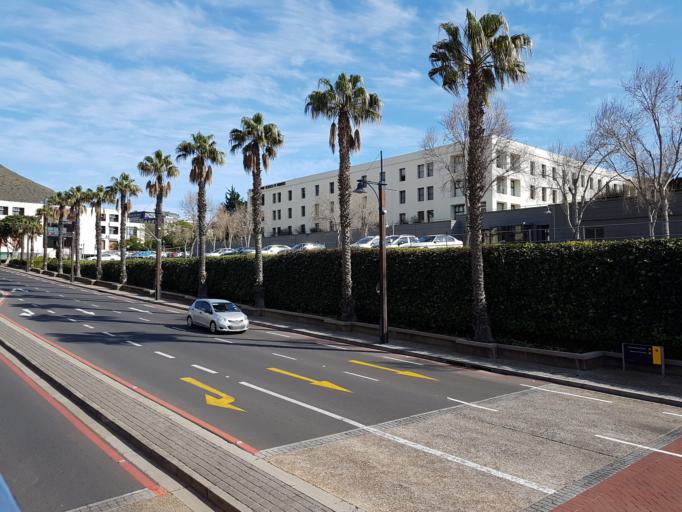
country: ZA
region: Western Cape
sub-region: City of Cape Town
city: Cape Town
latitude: -33.9081
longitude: 18.4165
